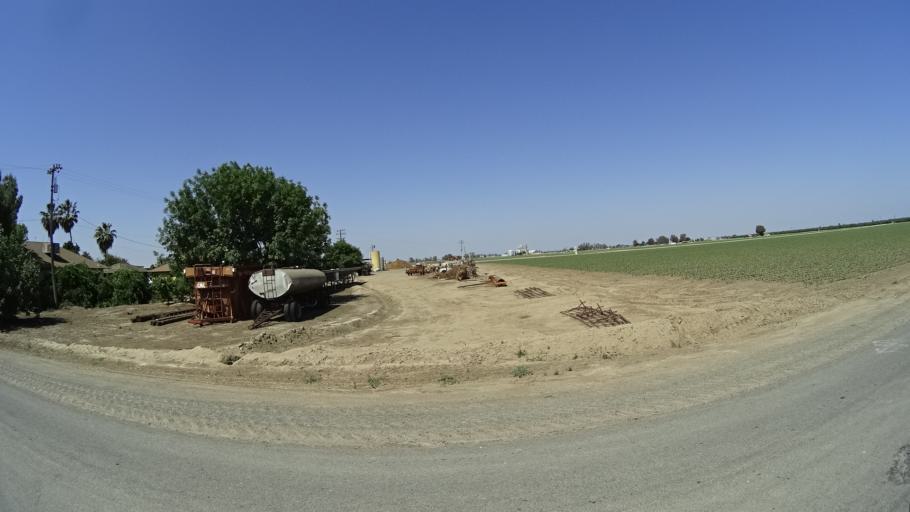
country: US
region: California
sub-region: Kings County
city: Home Garden
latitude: 36.2792
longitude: -119.6190
